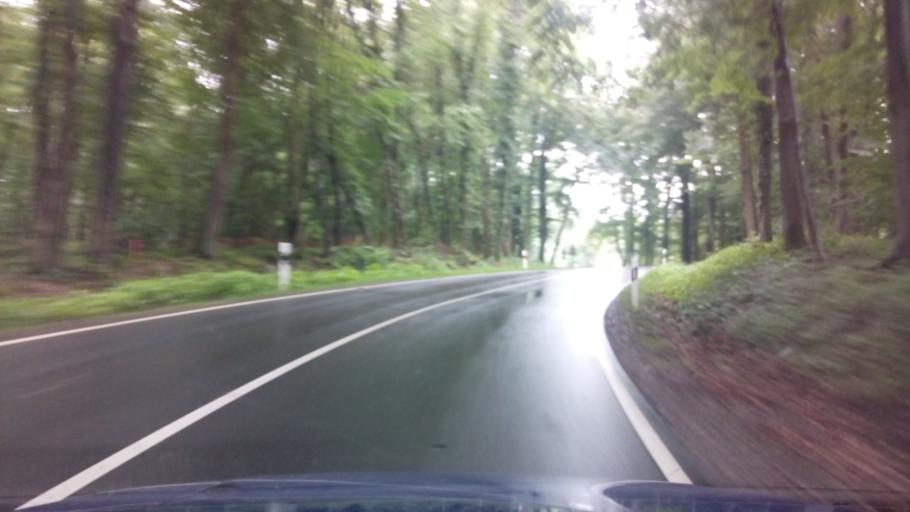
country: DE
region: Lower Saxony
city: Bad Essen
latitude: 52.3077
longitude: 8.3297
